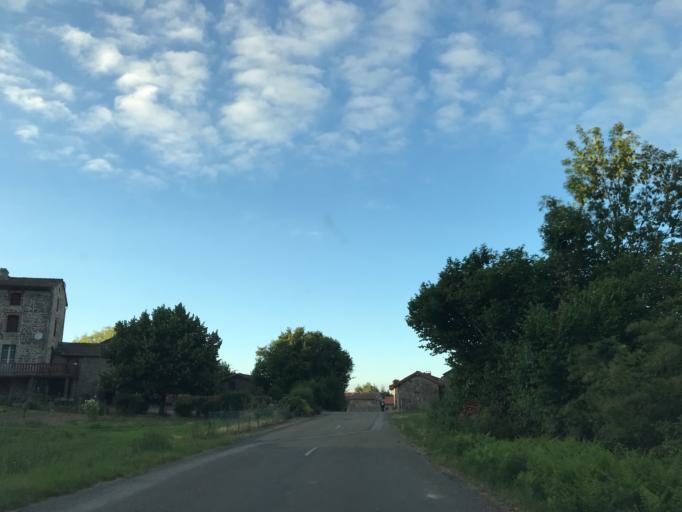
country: FR
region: Rhone-Alpes
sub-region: Departement de la Loire
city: Noiretable
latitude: 45.7855
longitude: 3.7773
